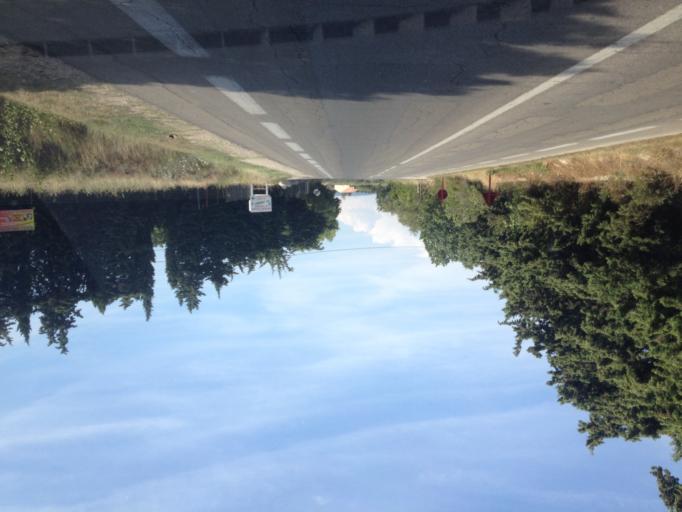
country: FR
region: Provence-Alpes-Cote d'Azur
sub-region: Departement du Vaucluse
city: Aubignan
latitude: 44.0812
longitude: 5.0381
